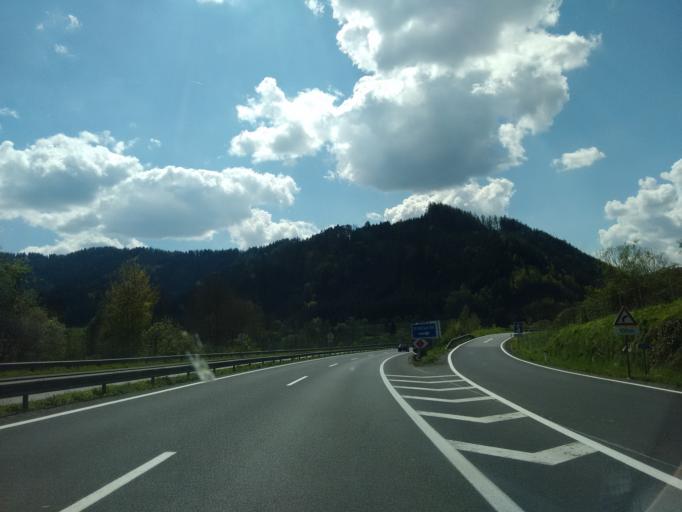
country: AT
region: Styria
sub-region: Politischer Bezirk Leoben
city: Sankt Michael in Obersteiermark
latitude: 47.3344
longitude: 15.0290
